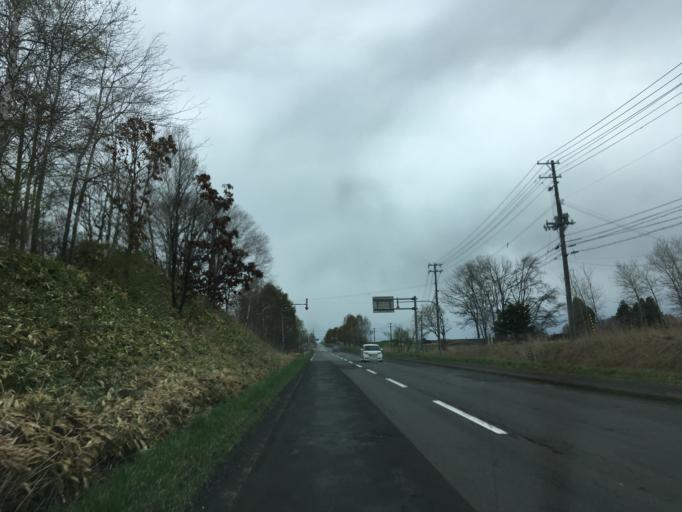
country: JP
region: Hokkaido
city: Chitose
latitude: 42.9124
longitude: 141.8109
